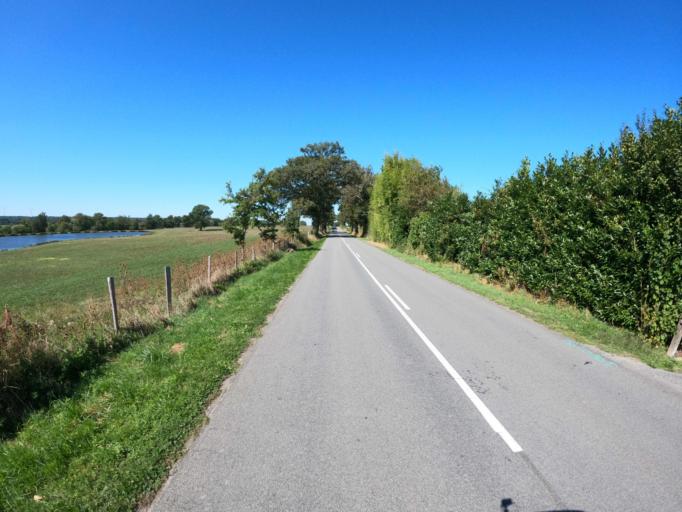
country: FR
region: Limousin
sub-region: Departement de la Haute-Vienne
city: Le Dorat
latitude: 46.2240
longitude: 1.0713
